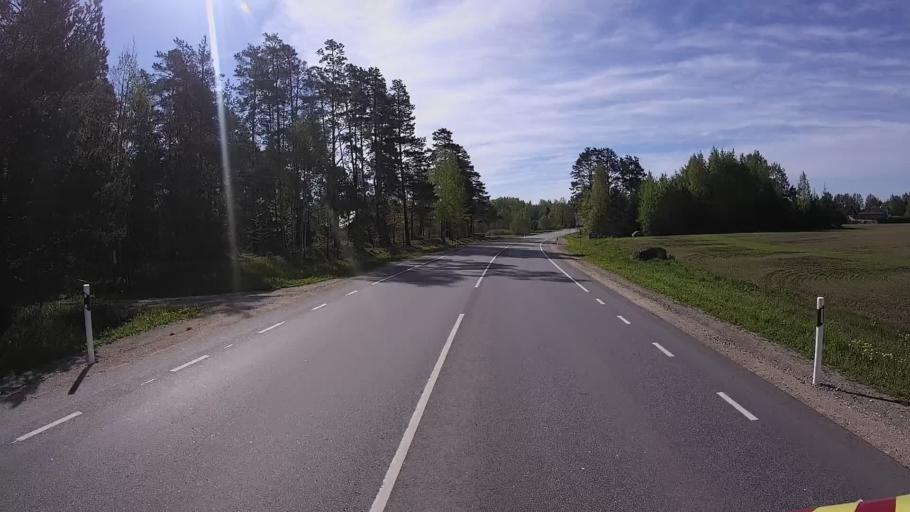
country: EE
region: Tartu
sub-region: UElenurme vald
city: Ulenurme
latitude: 58.3350
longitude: 26.9753
